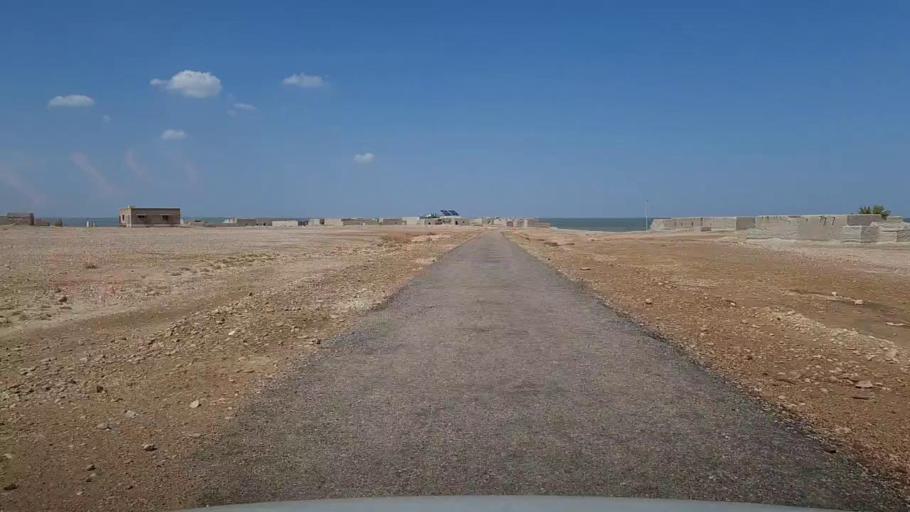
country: PK
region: Sindh
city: Bhan
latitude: 26.3861
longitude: 67.6312
